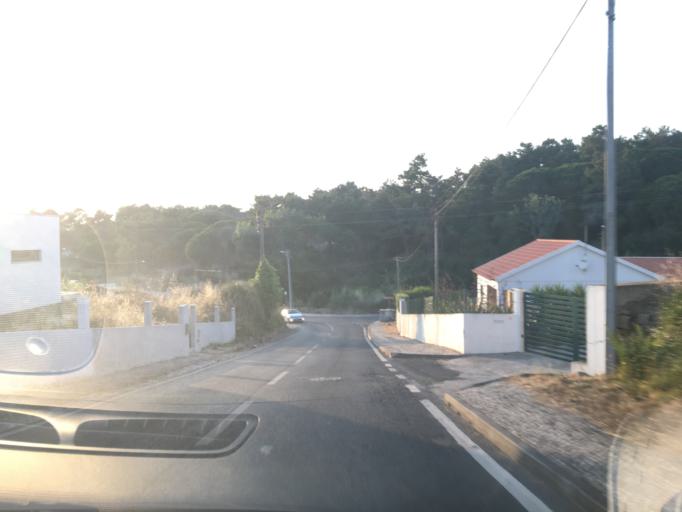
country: PT
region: Lisbon
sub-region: Sintra
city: Colares
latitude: 38.8282
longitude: -9.4382
